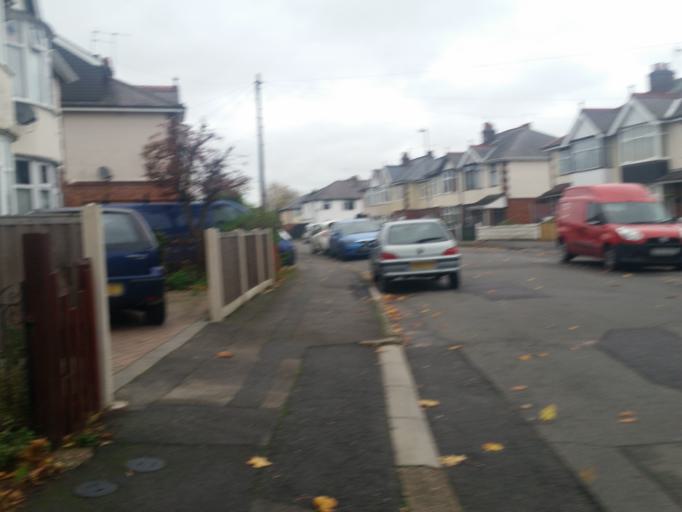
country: GB
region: England
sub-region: Derbyshire
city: Borrowash
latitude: 52.8954
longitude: -1.4237
